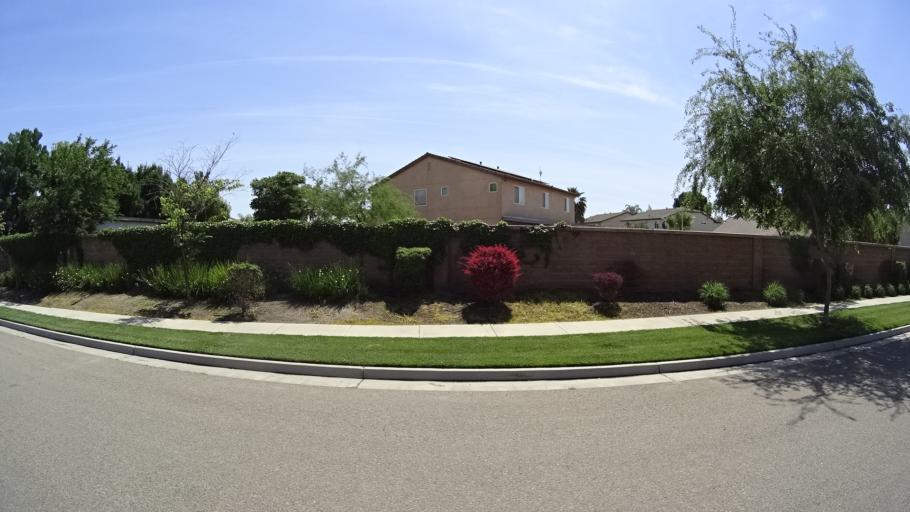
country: US
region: California
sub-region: Kings County
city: Lucerne
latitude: 36.3474
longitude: -119.6820
